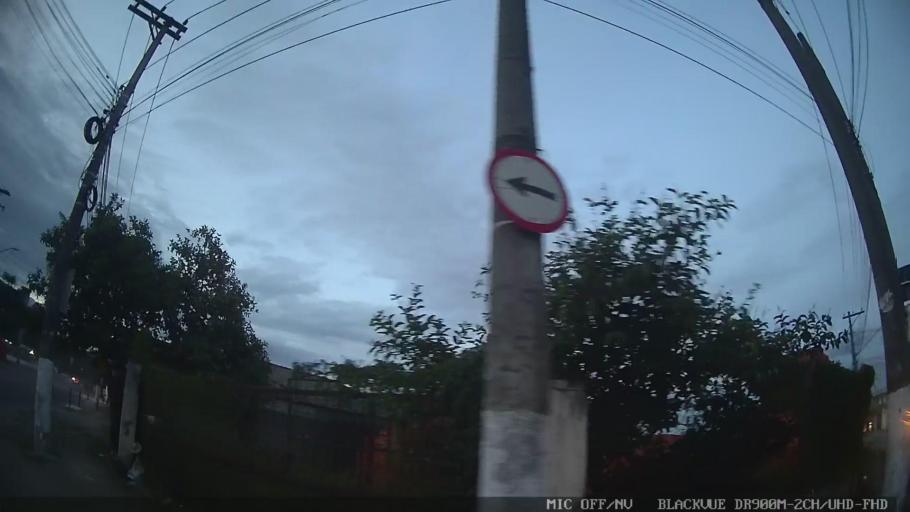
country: BR
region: Sao Paulo
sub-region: Itaquaquecetuba
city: Itaquaquecetuba
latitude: -23.4689
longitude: -46.3472
